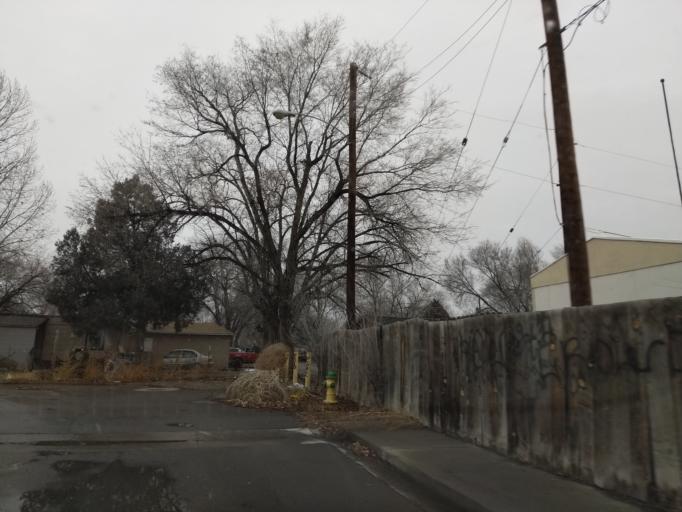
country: US
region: Colorado
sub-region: Mesa County
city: Grand Junction
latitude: 39.0753
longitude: -108.5260
